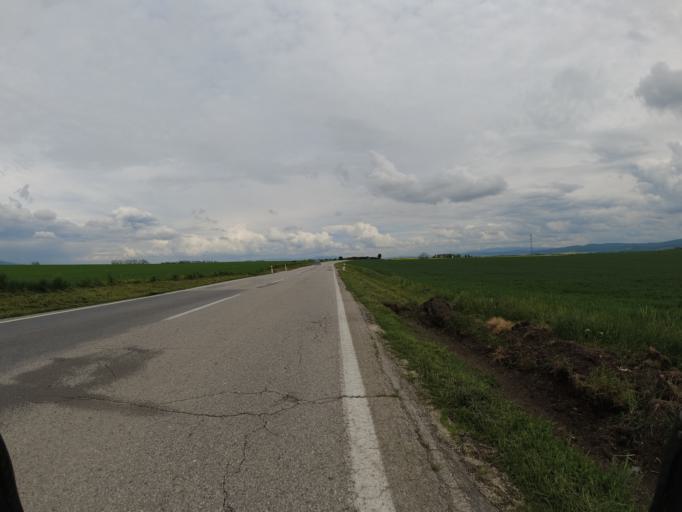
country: SK
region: Nitriansky
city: Banovce nad Bebravou
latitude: 48.5456
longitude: 18.1076
